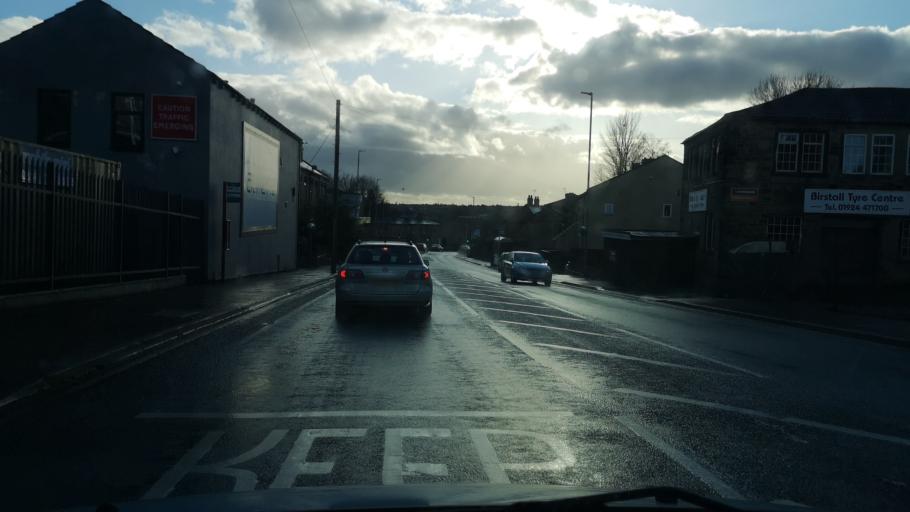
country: GB
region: England
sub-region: City and Borough of Leeds
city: Drighlington
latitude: 53.7334
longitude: -1.6571
